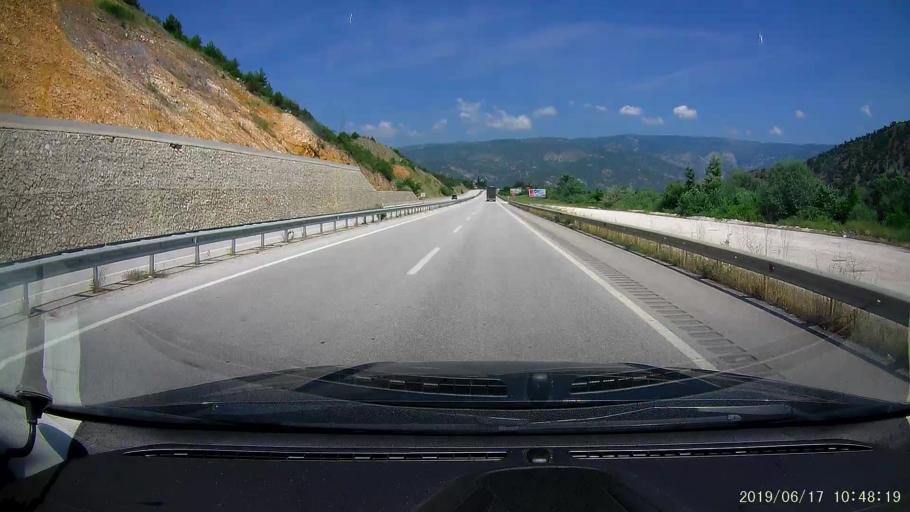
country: TR
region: Corum
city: Hacihamza
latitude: 41.0855
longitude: 34.4311
